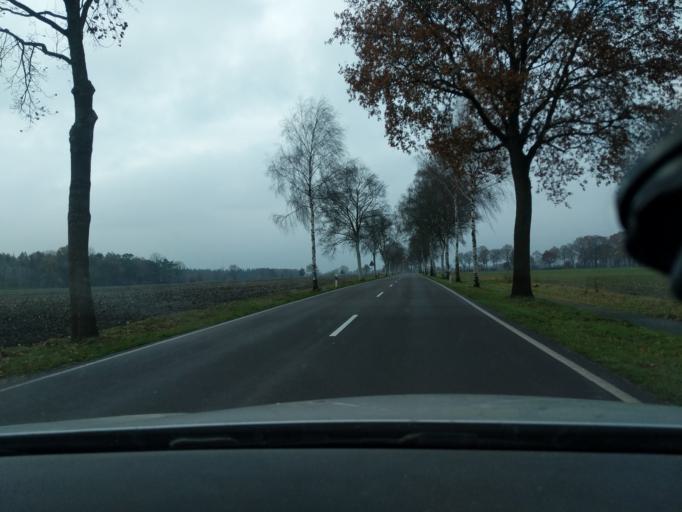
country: DE
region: Lower Saxony
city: Ahlerstedt
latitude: 53.3763
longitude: 9.4582
